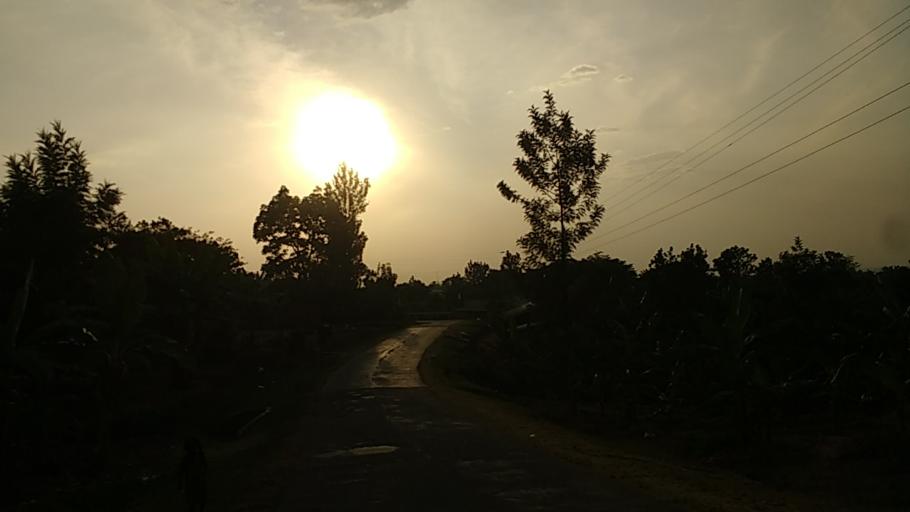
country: UG
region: Eastern Region
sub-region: Mbale District
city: Mbale
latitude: 1.0767
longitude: 34.2091
